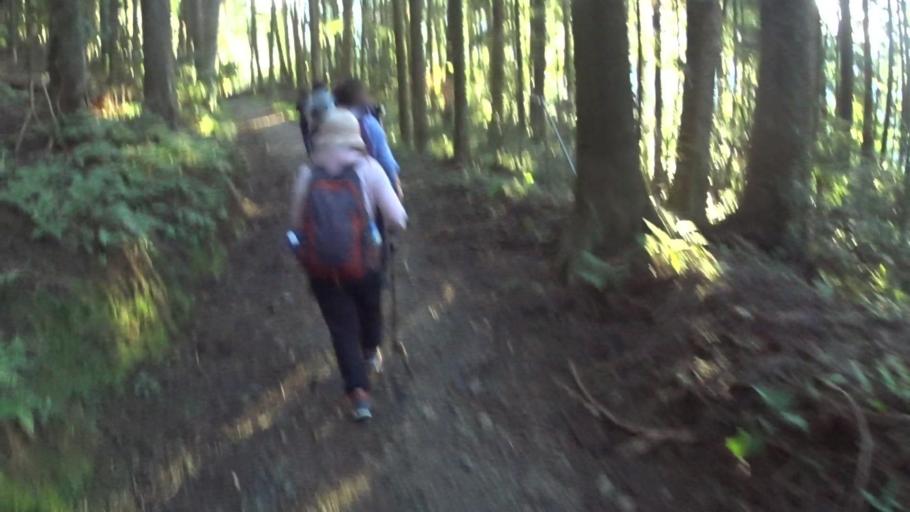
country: JP
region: Kyoto
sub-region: Kyoto-shi
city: Kamigyo-ku
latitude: 35.1082
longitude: 135.8275
